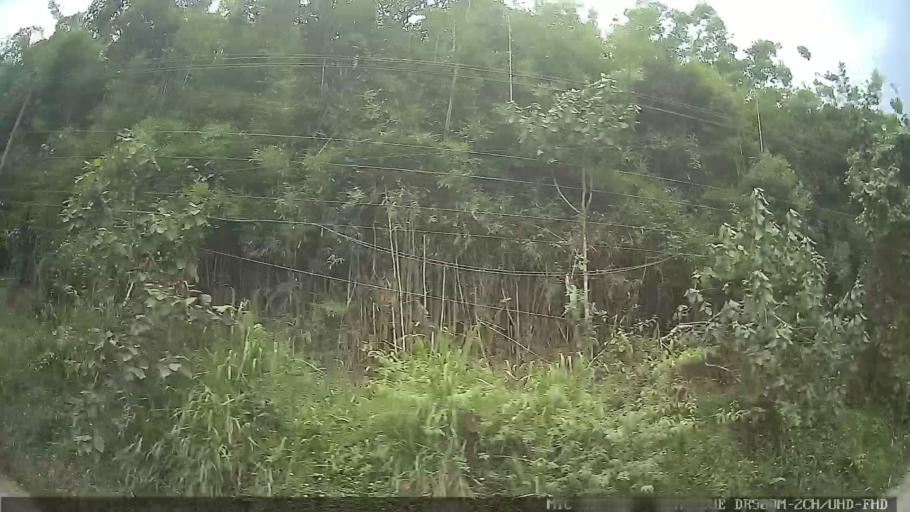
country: BR
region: Sao Paulo
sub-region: Rio Grande Da Serra
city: Rio Grande da Serra
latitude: -23.6896
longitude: -46.2978
